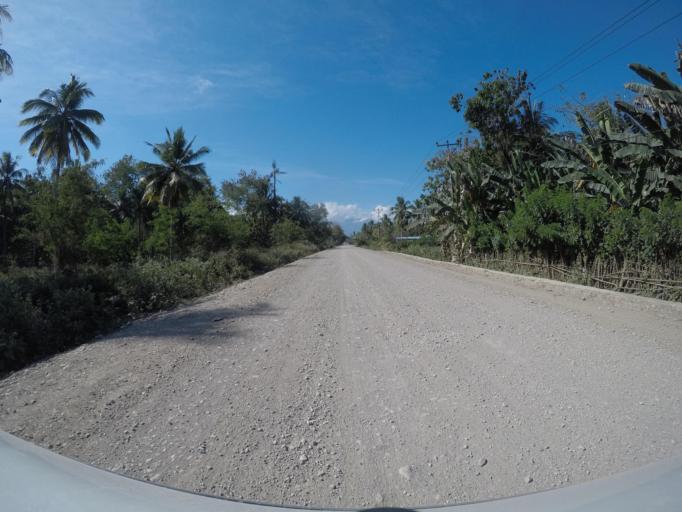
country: TL
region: Viqueque
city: Viqueque
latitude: -8.8583
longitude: 126.5100
